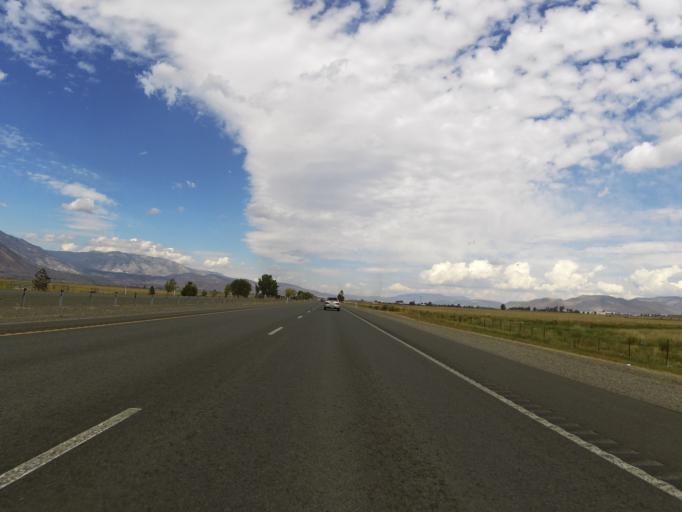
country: US
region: Nevada
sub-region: Douglas County
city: Minden
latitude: 38.9821
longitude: -119.7793
